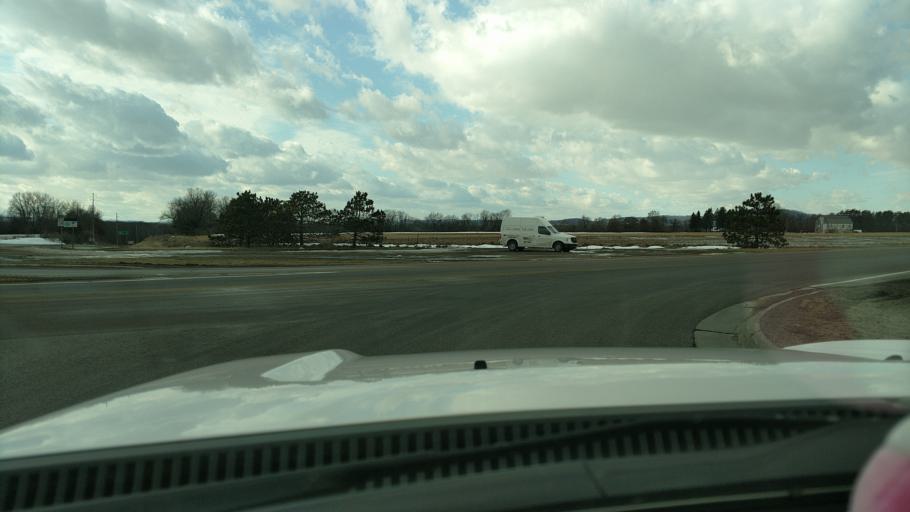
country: US
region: Minnesota
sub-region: Wabasha County
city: Wabasha
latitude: 44.4341
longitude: -92.0190
